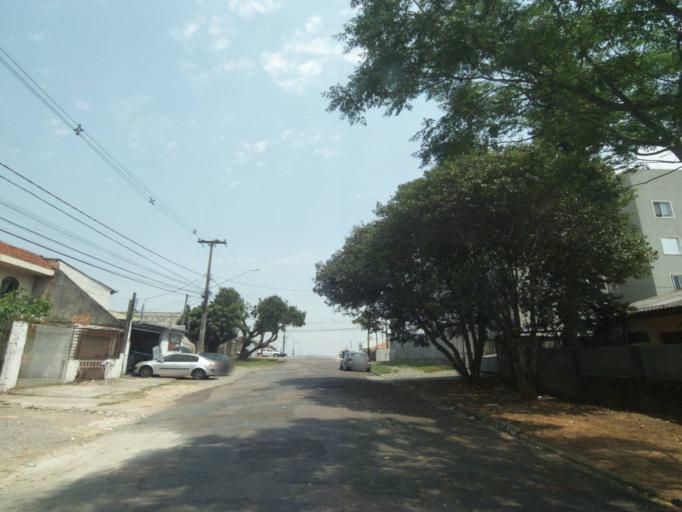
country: BR
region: Parana
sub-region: Sao Jose Dos Pinhais
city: Sao Jose dos Pinhais
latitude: -25.5326
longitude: -49.2456
